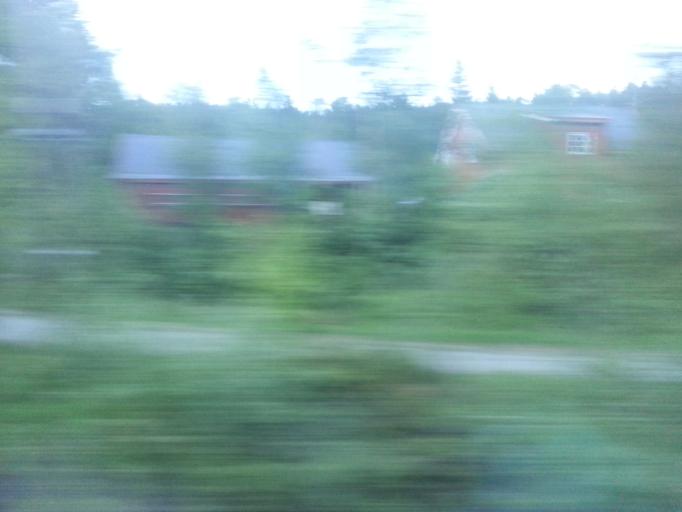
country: NO
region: Oppland
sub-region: Dovre
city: Dombas
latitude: 62.0744
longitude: 9.1312
